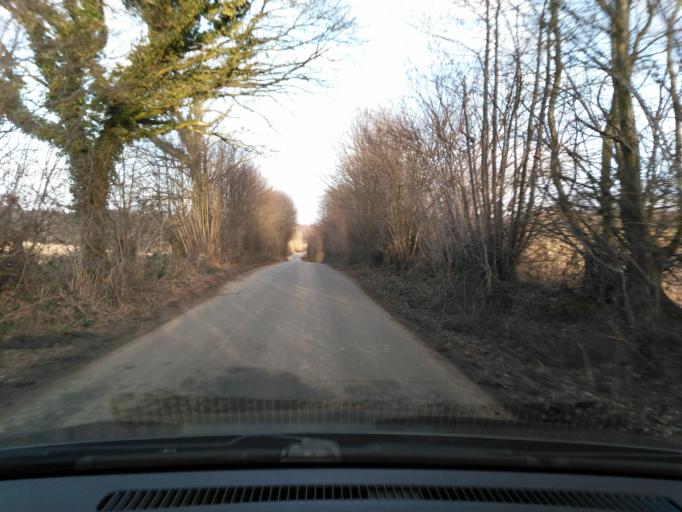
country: DE
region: Schleswig-Holstein
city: Honigsee
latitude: 54.2680
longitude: 10.1900
